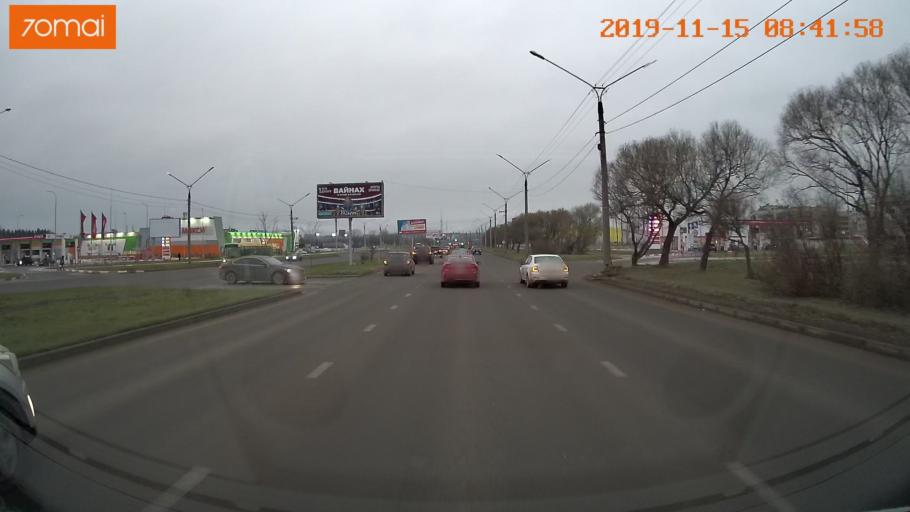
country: RU
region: Vologda
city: Cherepovets
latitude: 59.0995
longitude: 37.9104
